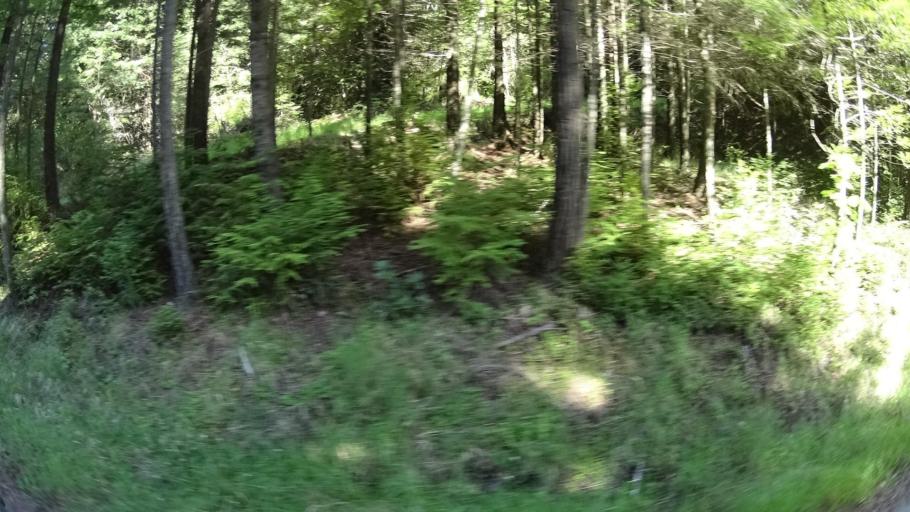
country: US
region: California
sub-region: Humboldt County
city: Rio Dell
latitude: 40.4599
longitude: -124.0647
